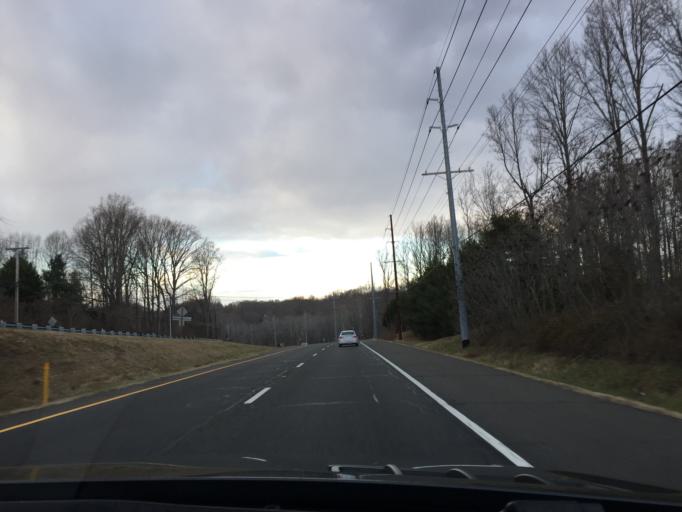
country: US
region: Maryland
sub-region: Calvert County
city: Dunkirk Town Center
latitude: 38.7055
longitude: -76.6482
